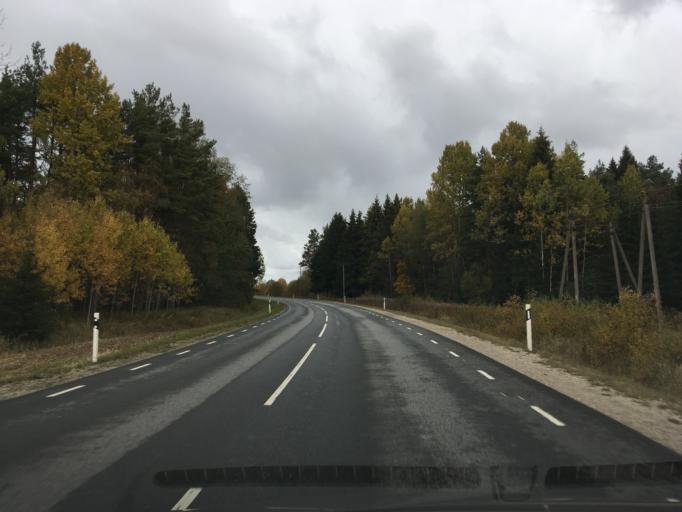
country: EE
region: Harju
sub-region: Anija vald
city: Kehra
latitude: 59.3178
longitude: 25.3437
